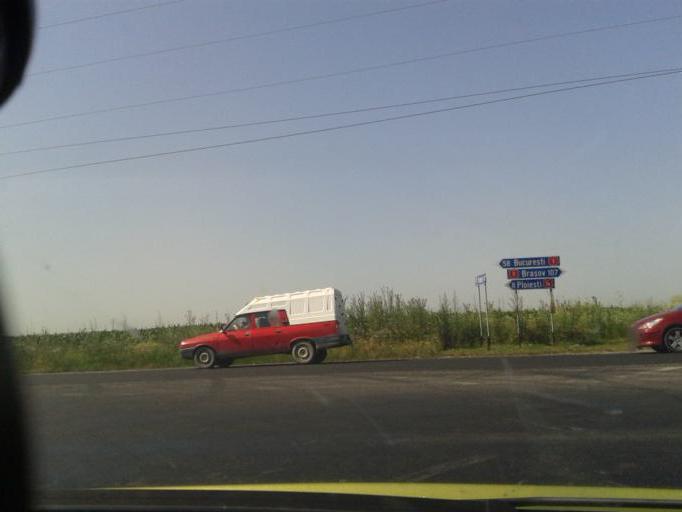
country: RO
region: Prahova
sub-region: Comuna Paulesti
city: Gageni
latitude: 44.9781
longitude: 25.9405
